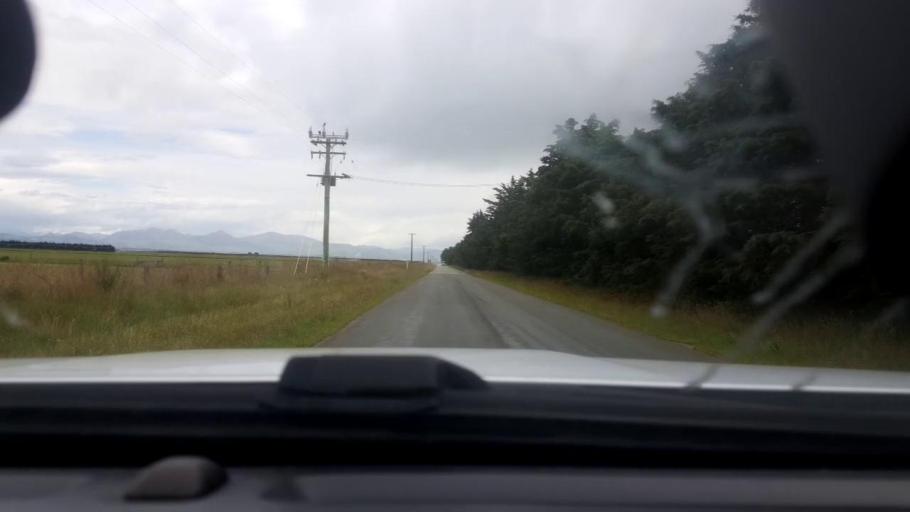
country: NZ
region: Canterbury
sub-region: Timaru District
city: Timaru
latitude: -44.1585
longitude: 171.4023
